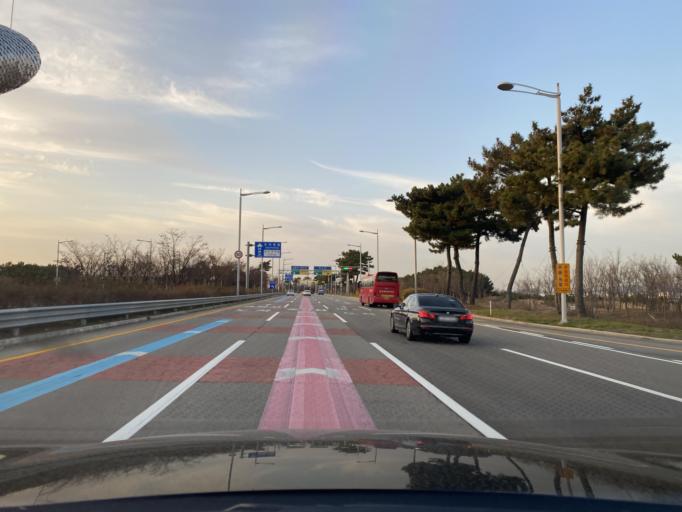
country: KR
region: Incheon
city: Incheon
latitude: 37.4440
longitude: 126.4656
